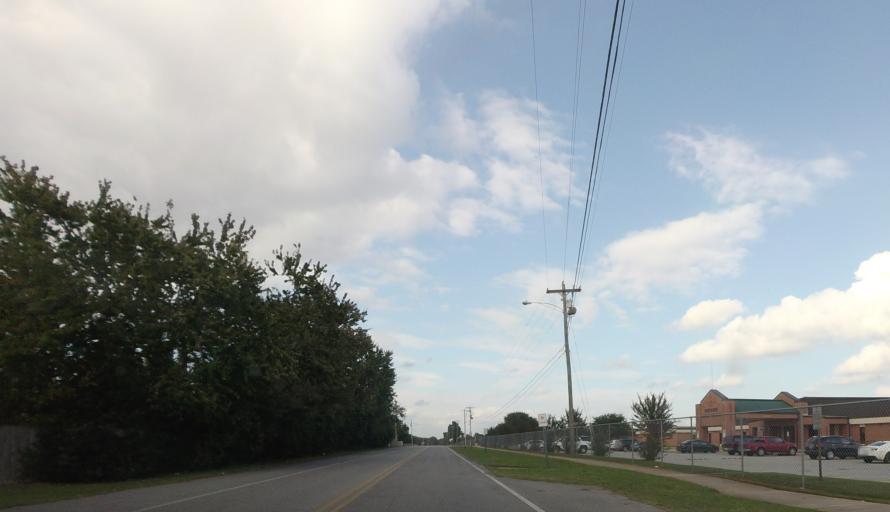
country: US
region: Georgia
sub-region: Houston County
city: Centerville
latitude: 32.6345
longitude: -83.6456
